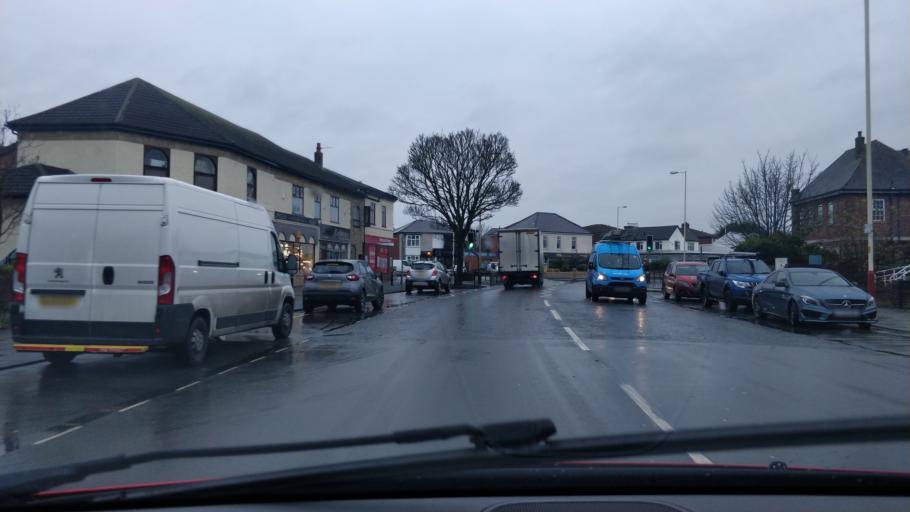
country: GB
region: England
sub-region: Sefton
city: Southport
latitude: 53.6023
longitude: -3.0334
